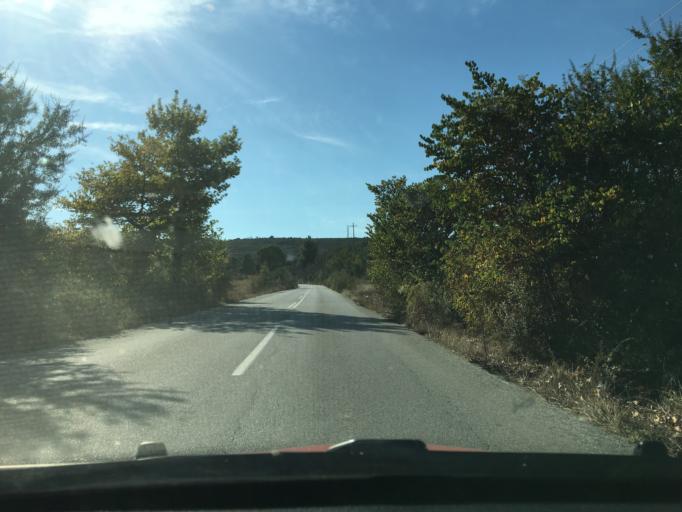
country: GR
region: Central Macedonia
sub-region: Nomos Chalkidikis
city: Ierissos
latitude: 40.3920
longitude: 23.7759
